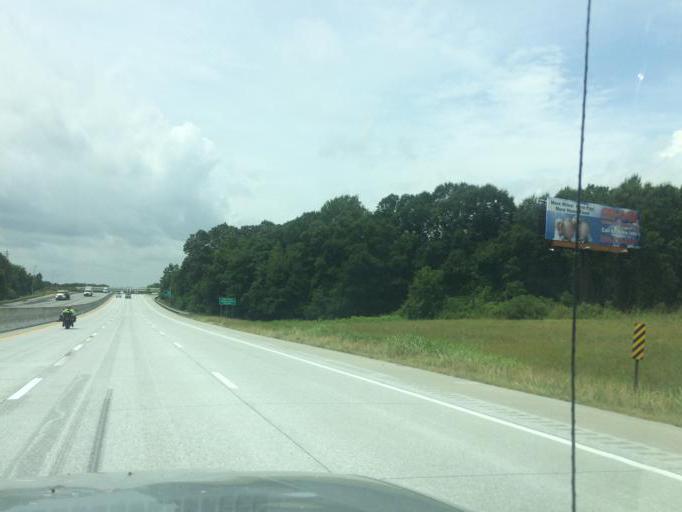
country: US
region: South Carolina
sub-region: Anderson County
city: Northlake
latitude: 34.6350
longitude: -82.5925
